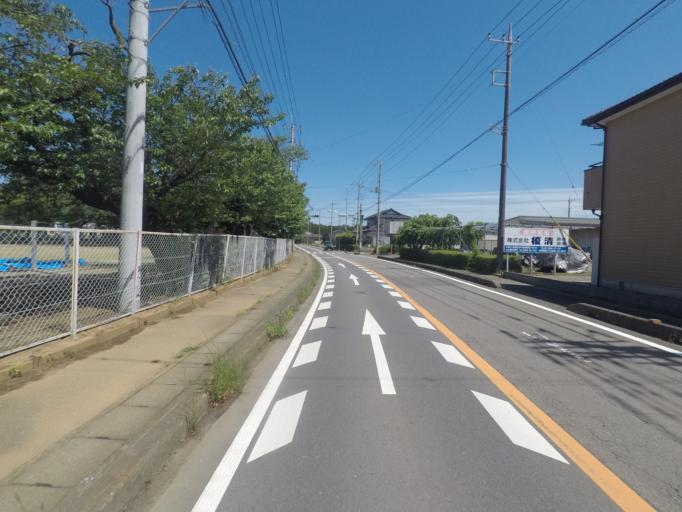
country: JP
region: Ibaraki
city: Ami
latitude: 36.0977
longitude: 140.2443
